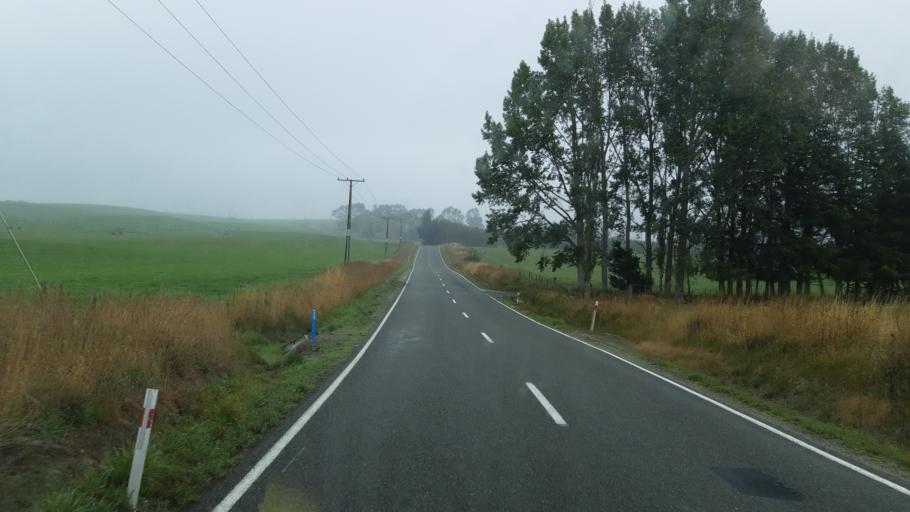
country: NZ
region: Otago
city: Oamaru
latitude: -44.9203
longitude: 170.8182
